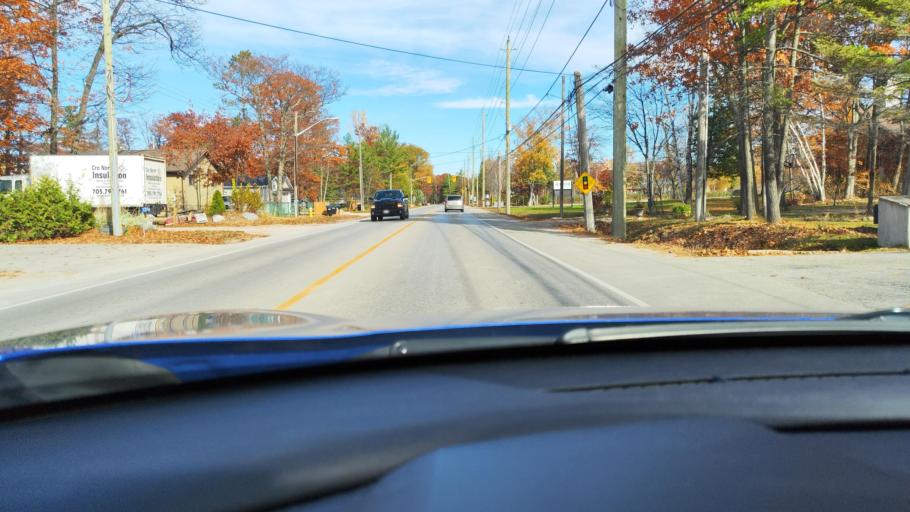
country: CA
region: Ontario
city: Wasaga Beach
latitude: 44.5104
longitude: -80.0270
